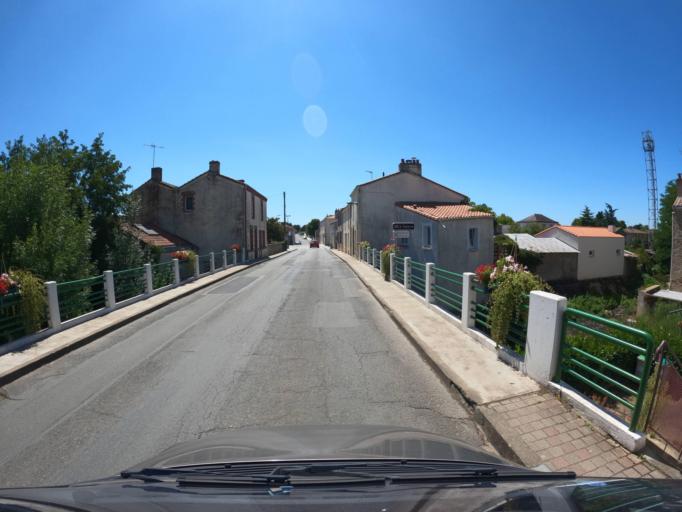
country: FR
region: Pays de la Loire
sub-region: Departement de la Vendee
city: Saint-Philbert-de-Bouaine
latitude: 46.9845
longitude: -1.5213
